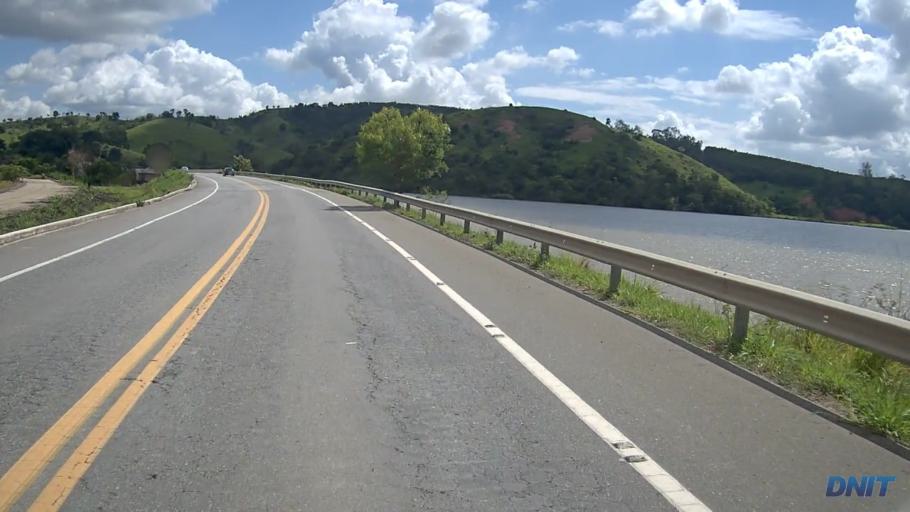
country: BR
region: Minas Gerais
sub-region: Governador Valadares
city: Governador Valadares
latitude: -19.0412
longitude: -42.1491
